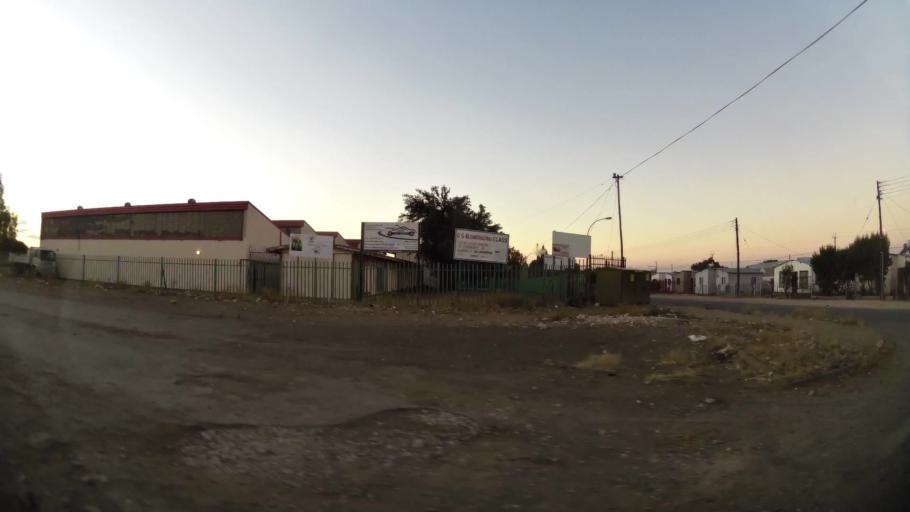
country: ZA
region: Northern Cape
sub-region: Frances Baard District Municipality
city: Kimberley
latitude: -28.7177
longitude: 24.7671
